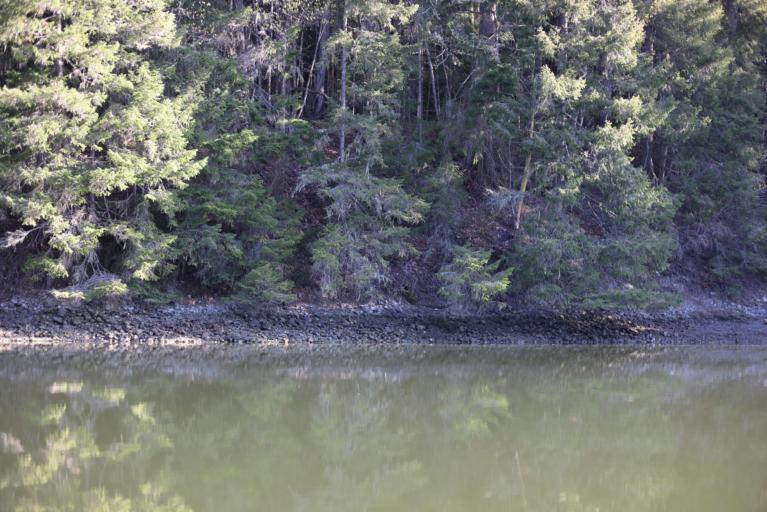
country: CA
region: British Columbia
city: Langford
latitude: 48.5607
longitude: -123.4719
